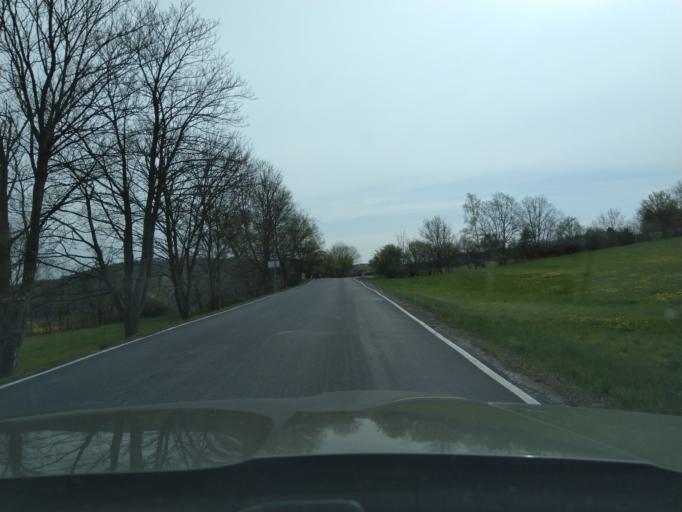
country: CZ
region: Plzensky
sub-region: Okres Klatovy
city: Susice
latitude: 49.2476
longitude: 13.5699
